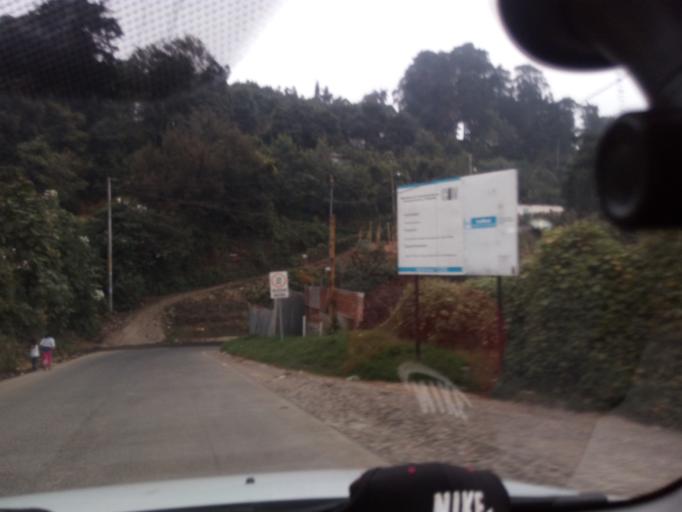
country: GT
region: Sacatepequez
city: Antigua Guatemala
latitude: 14.5820
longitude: -90.7125
